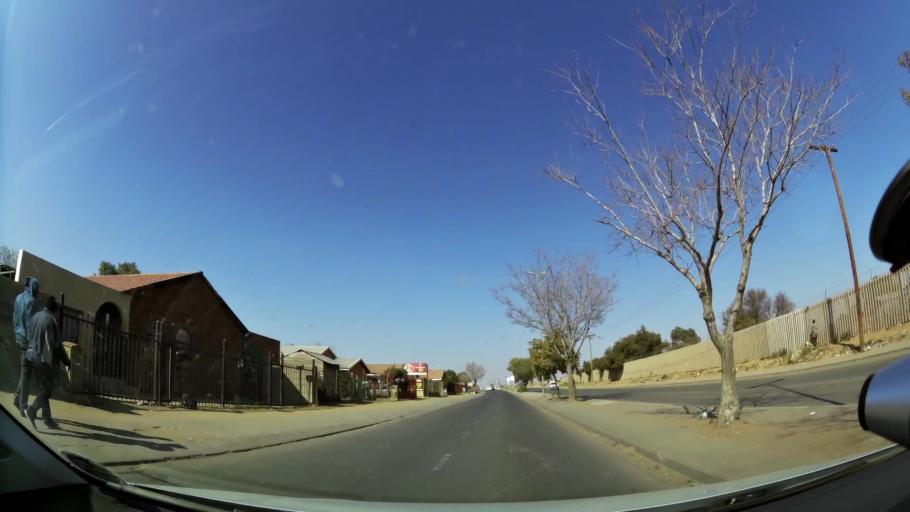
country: ZA
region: Orange Free State
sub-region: Mangaung Metropolitan Municipality
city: Bloemfontein
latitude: -29.1564
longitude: 26.2542
